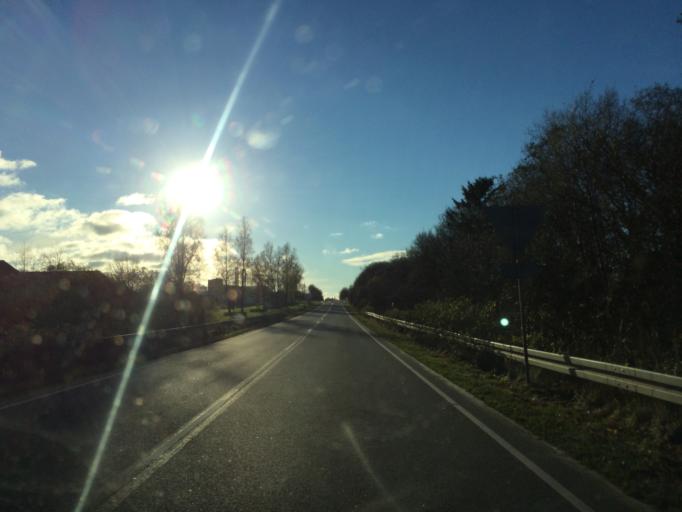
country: DK
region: Central Jutland
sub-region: Herning Kommune
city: Kibaek
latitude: 56.0343
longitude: 8.8639
